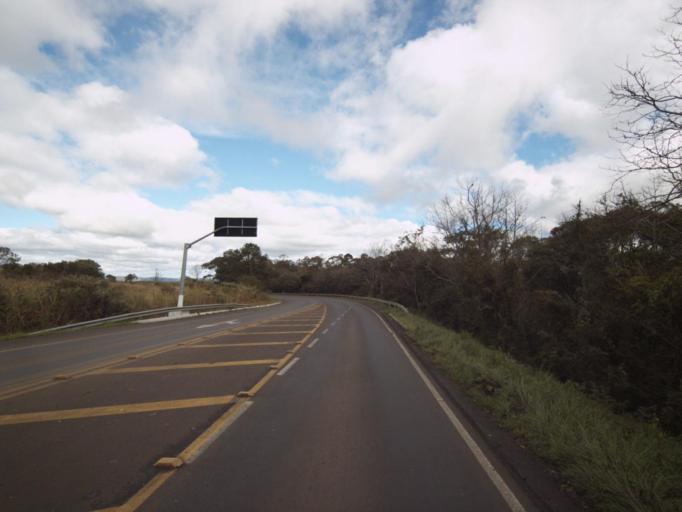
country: BR
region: Santa Catarina
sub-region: Concordia
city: Concordia
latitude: -27.3163
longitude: -51.9868
